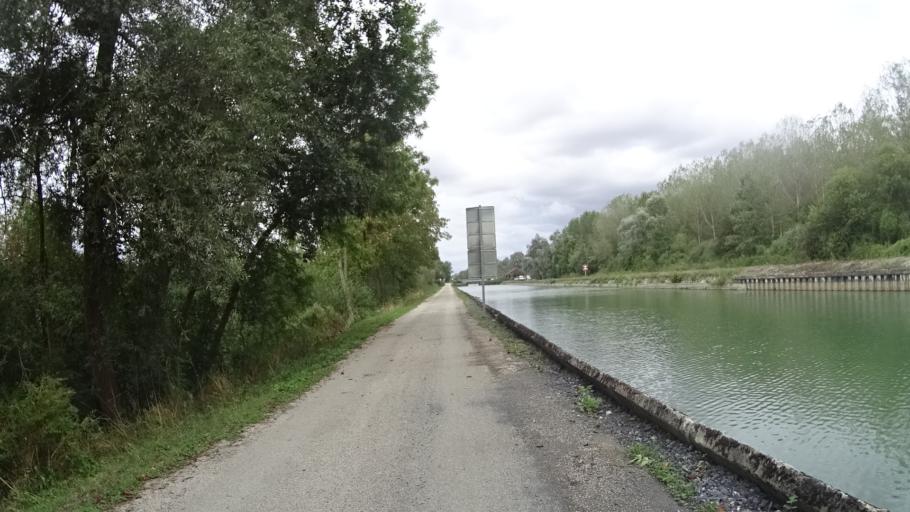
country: FR
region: Picardie
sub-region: Departement de l'Aisne
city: La Fere
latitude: 49.6880
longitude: 3.3663
